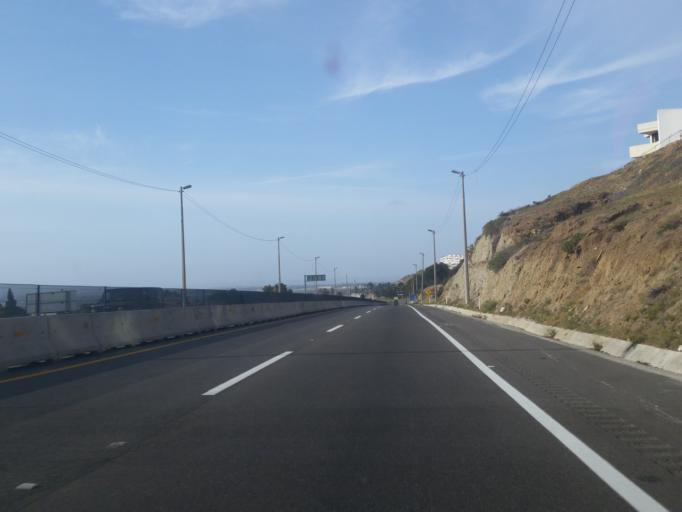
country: MX
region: Baja California
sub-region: Tijuana
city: La Esperanza [Granjas Familiares]
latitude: 32.5213
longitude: -117.1077
